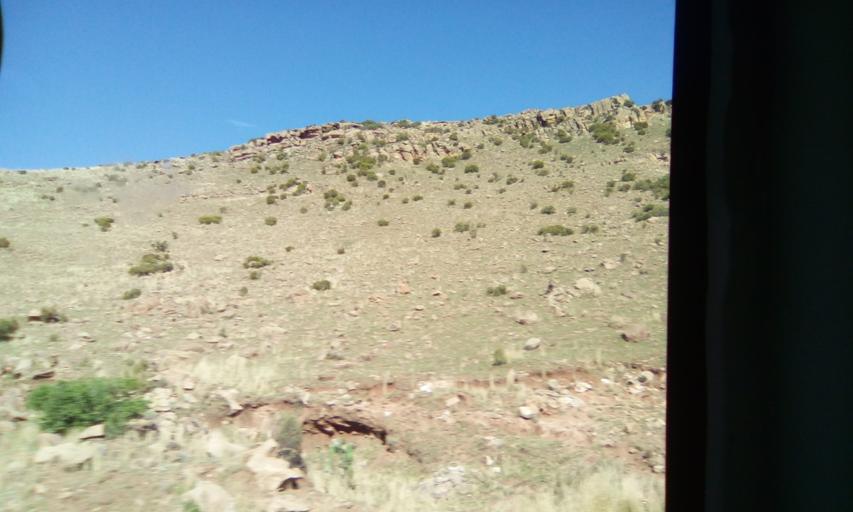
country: LS
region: Qacha's Nek
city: Qacha's Nek
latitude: -30.0414
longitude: 28.3498
